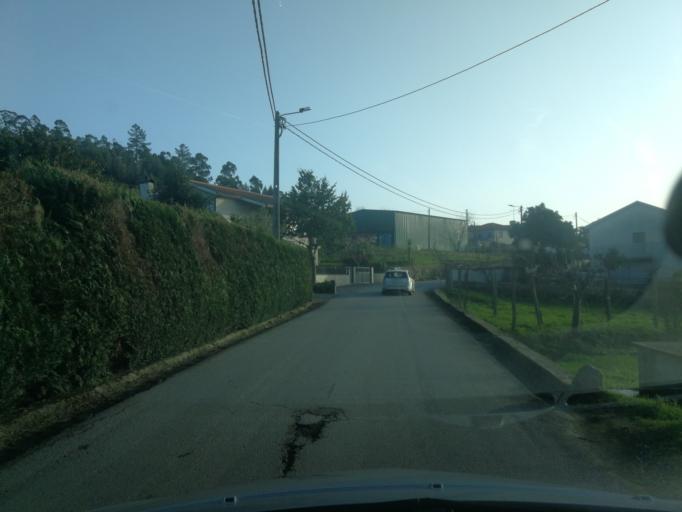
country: PT
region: Braga
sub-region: Barcelos
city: Galegos
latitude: 41.5157
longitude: -8.5613
